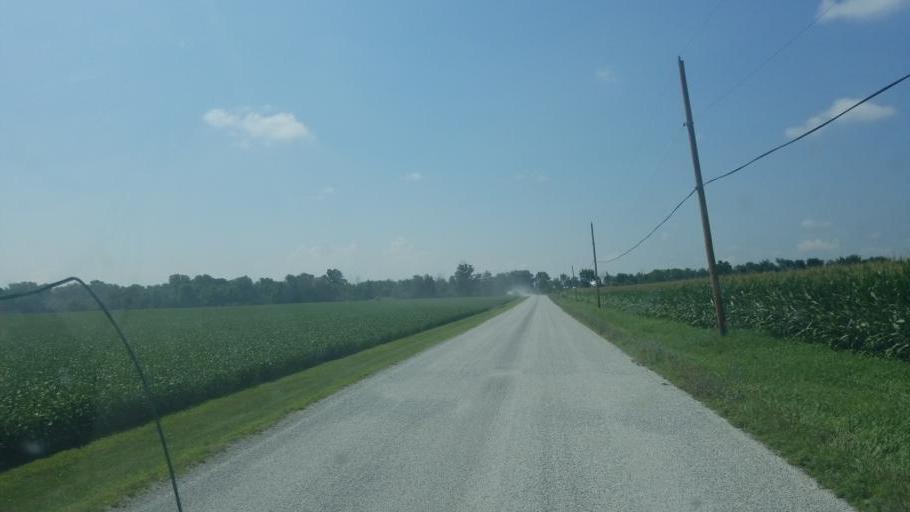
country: US
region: Ohio
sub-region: Hardin County
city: Ada
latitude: 40.6886
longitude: -83.7306
